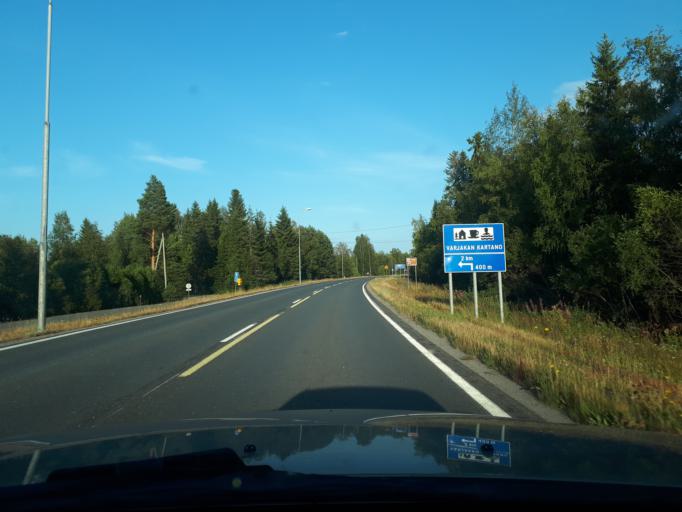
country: FI
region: Northern Ostrobothnia
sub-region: Oulu
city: Oulunsalo
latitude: 64.9748
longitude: 25.3182
